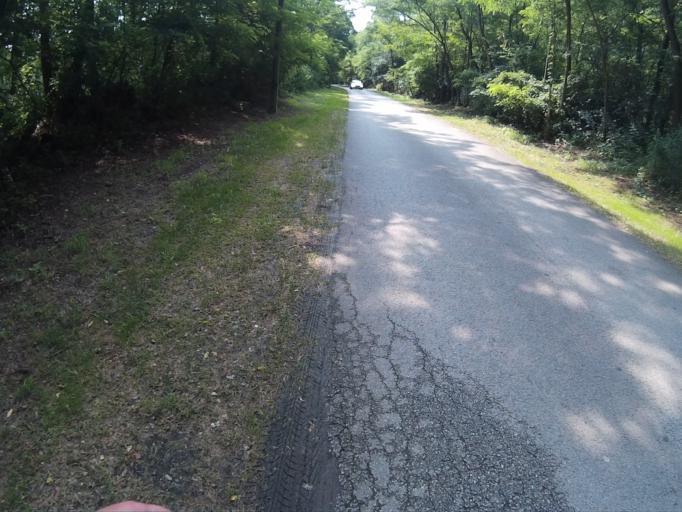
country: HU
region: Veszprem
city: Papa
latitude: 47.2830
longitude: 17.5809
